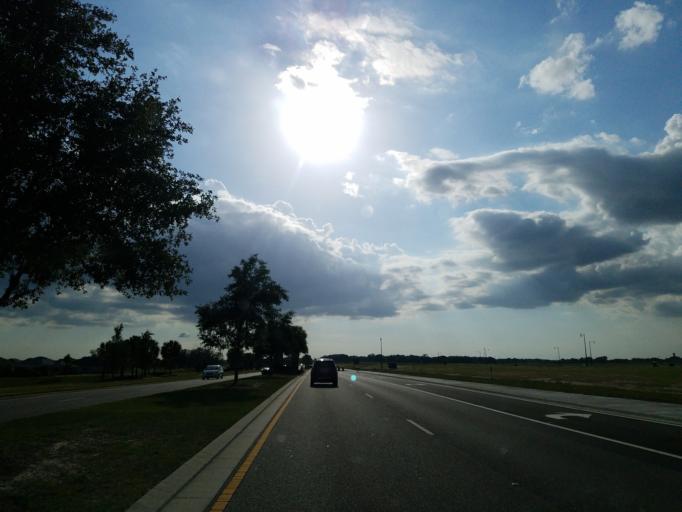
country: US
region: Florida
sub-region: Sumter County
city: Wildwood
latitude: 28.8654
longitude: -82.0013
